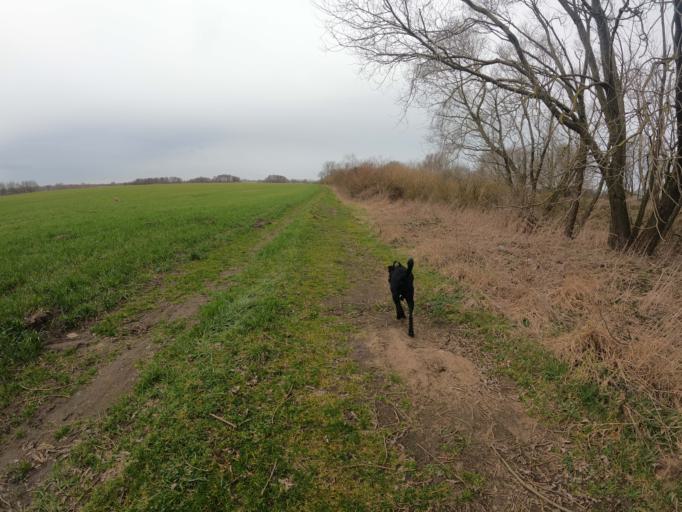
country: PL
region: West Pomeranian Voivodeship
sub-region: Powiat gryficki
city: Trzebiatow
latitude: 54.0739
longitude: 15.2490
